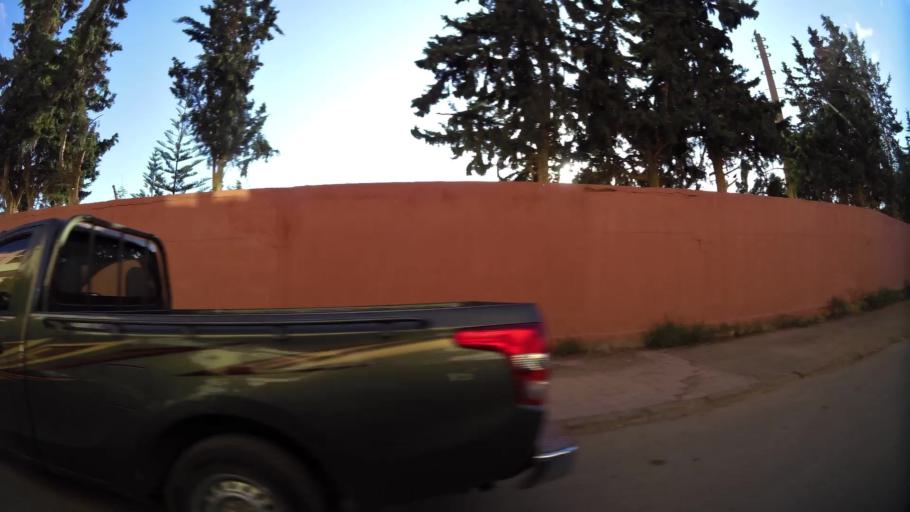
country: MA
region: Oriental
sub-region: Berkane-Taourirt
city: Berkane
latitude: 34.9291
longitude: -2.3262
